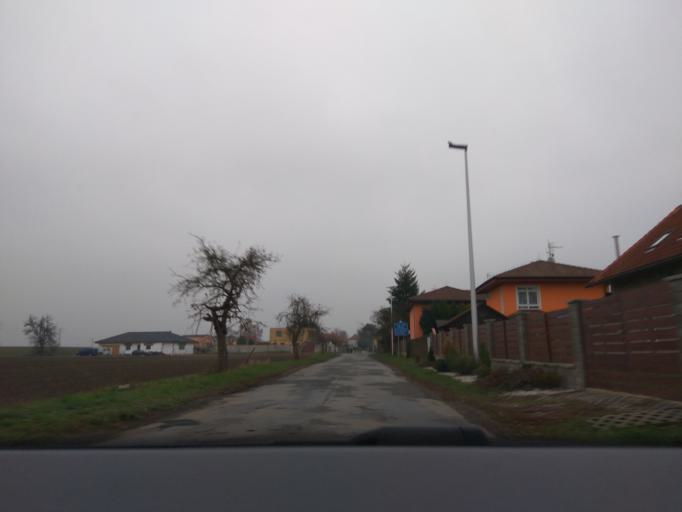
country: CZ
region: Praha
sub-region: Praha 19
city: Kbely
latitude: 50.1613
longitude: 14.5713
